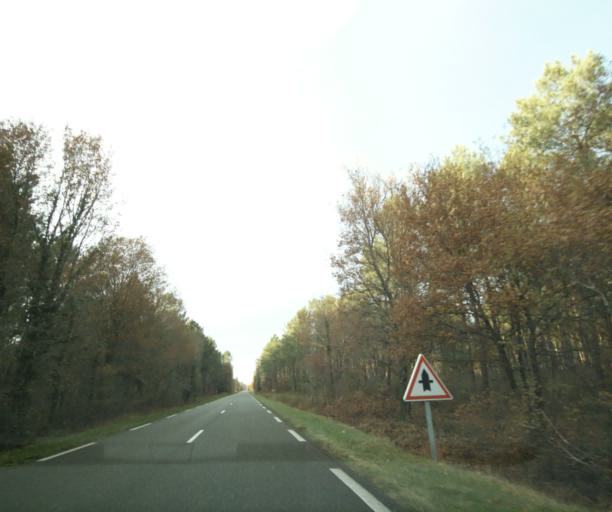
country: FR
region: Aquitaine
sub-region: Departement des Landes
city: Gabarret
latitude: 44.0430
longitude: -0.0372
